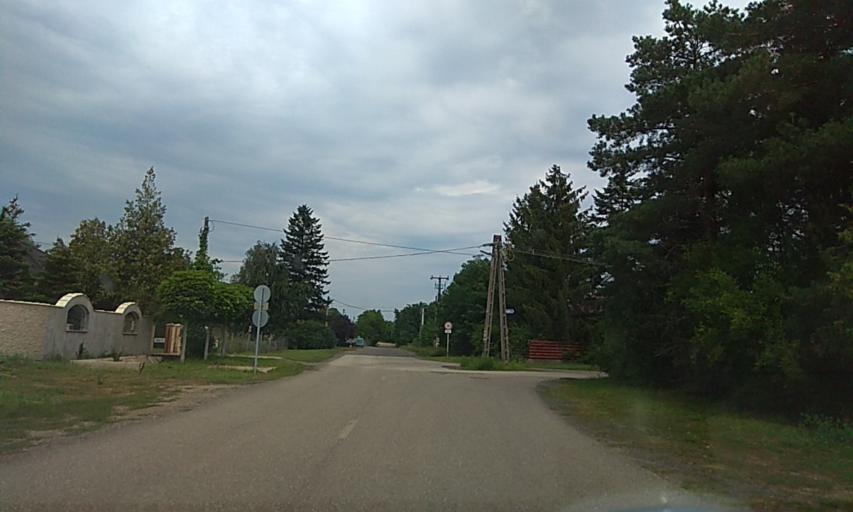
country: HU
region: Szabolcs-Szatmar-Bereg
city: Kotaj
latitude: 48.0029
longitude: 21.7088
